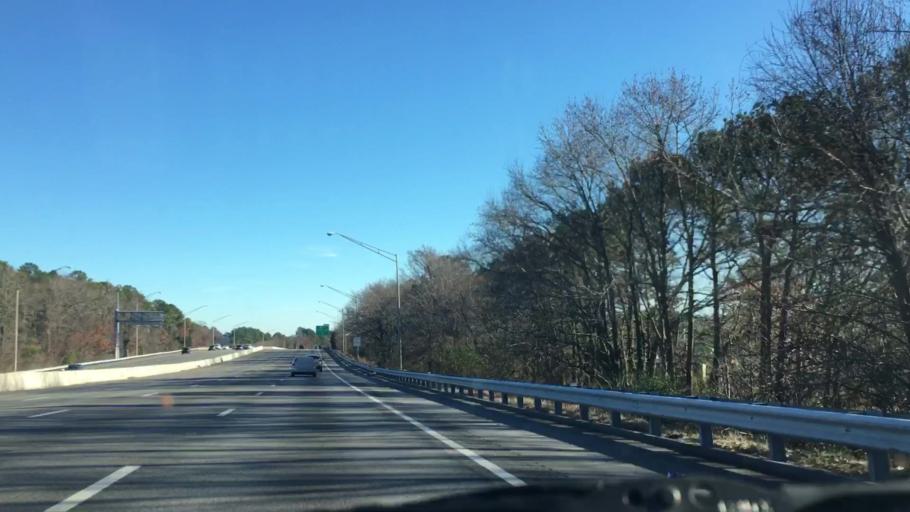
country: US
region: Virginia
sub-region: City of Virginia Beach
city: Virginia Beach
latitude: 36.8396
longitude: -76.0518
